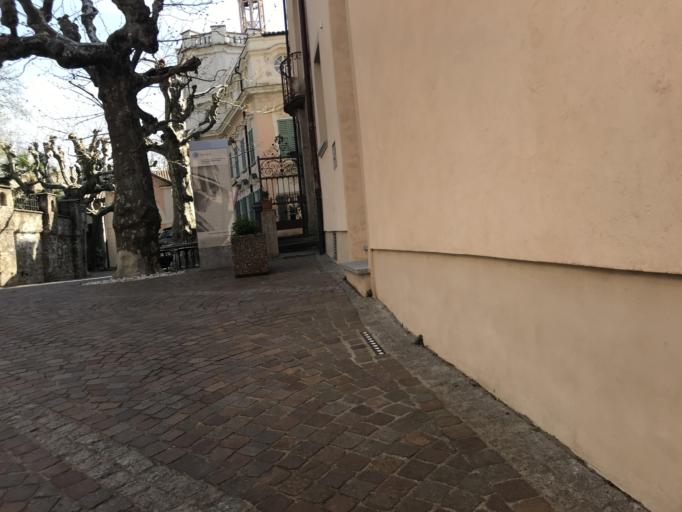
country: CH
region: Ticino
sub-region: Lugano District
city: Montagnola
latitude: 45.9830
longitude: 8.9185
